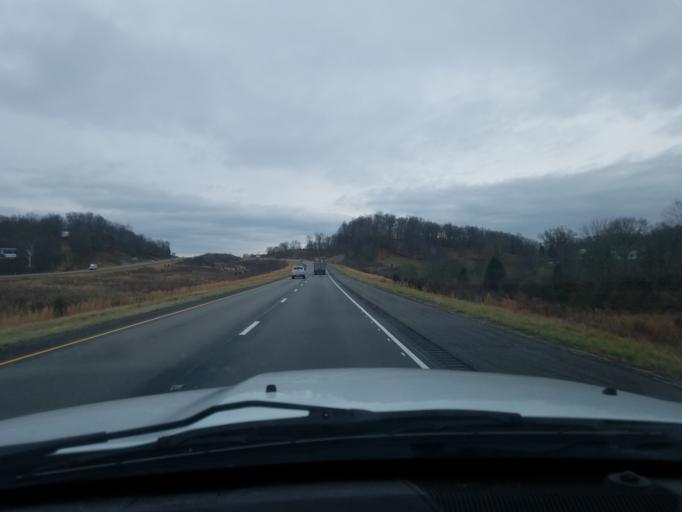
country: US
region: Indiana
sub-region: Dubois County
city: Ferdinand
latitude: 38.2034
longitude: -86.8417
